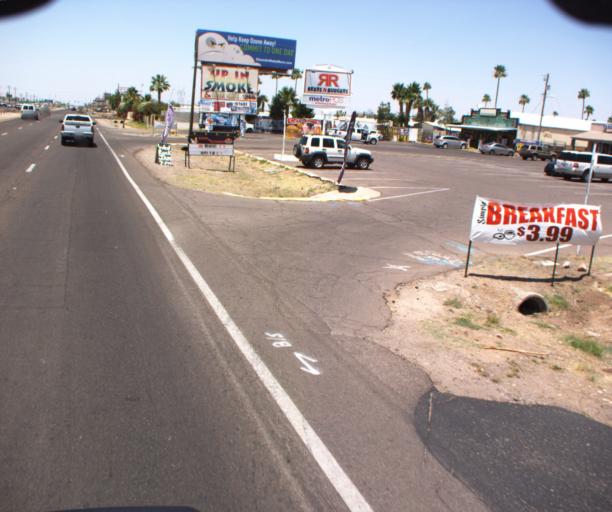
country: US
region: Arizona
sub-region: Pinal County
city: Apache Junction
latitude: 33.4154
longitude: -111.6087
